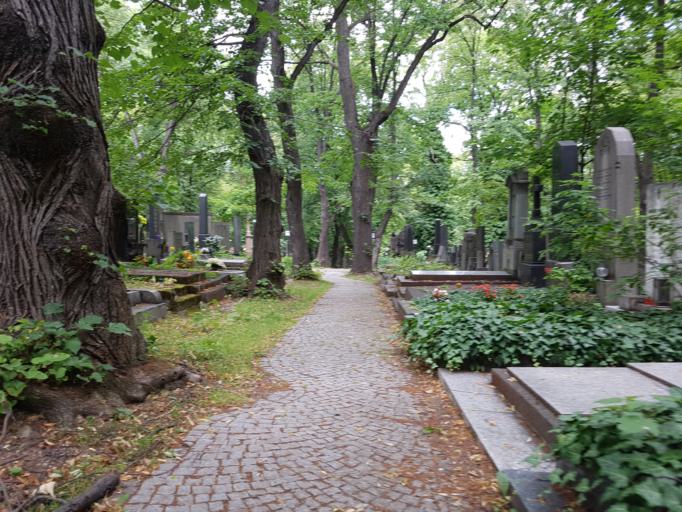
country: CZ
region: Praha
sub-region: Praha 8
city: Karlin
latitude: 50.0797
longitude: 14.4662
